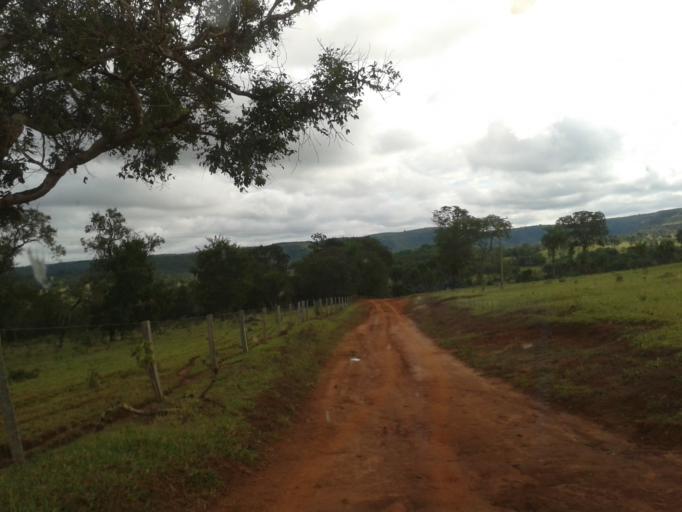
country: BR
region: Minas Gerais
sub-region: Campina Verde
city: Campina Verde
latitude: -19.4863
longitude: -49.6162
